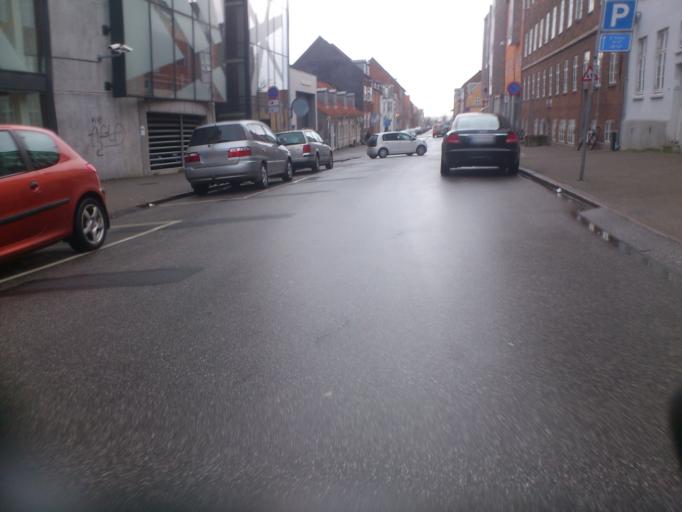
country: DK
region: South Denmark
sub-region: Fredericia Kommune
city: Fredericia
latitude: 55.5651
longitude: 9.7577
